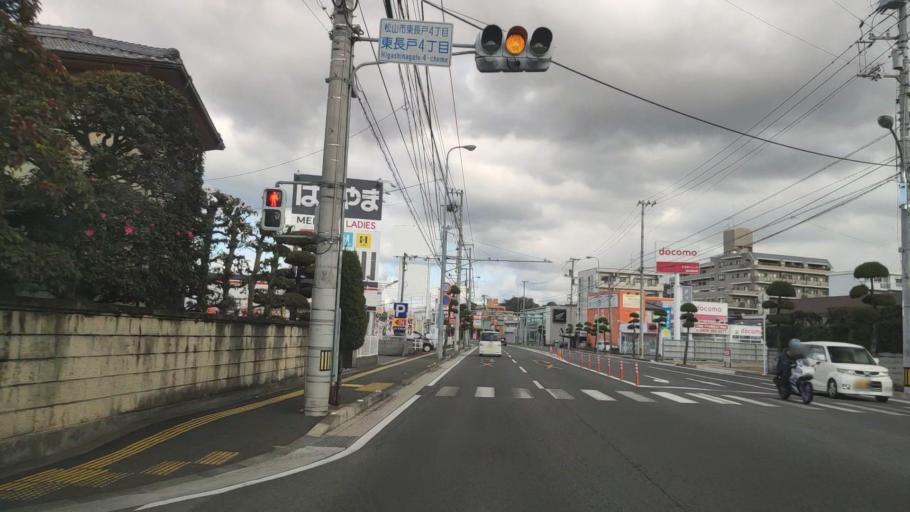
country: JP
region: Ehime
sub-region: Shikoku-chuo Shi
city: Matsuyama
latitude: 33.8688
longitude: 132.7518
